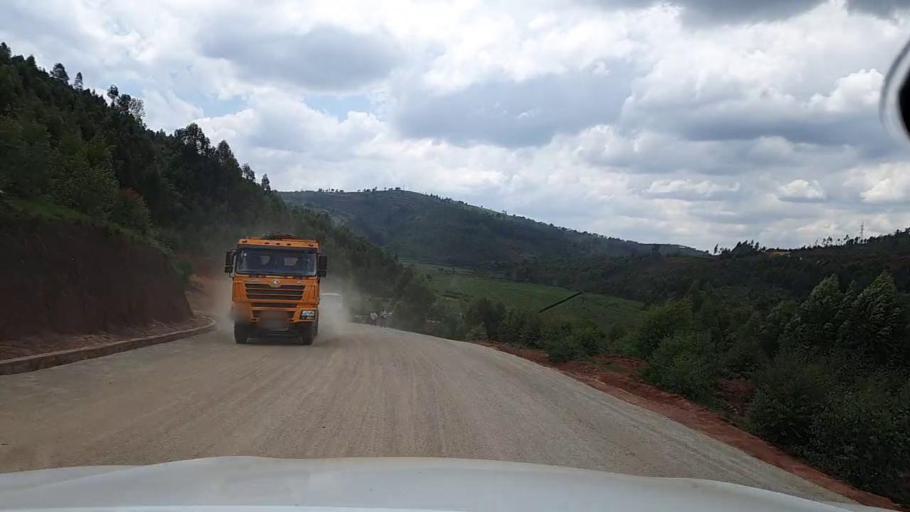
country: RW
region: Southern Province
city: Butare
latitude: -2.6959
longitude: 29.5548
